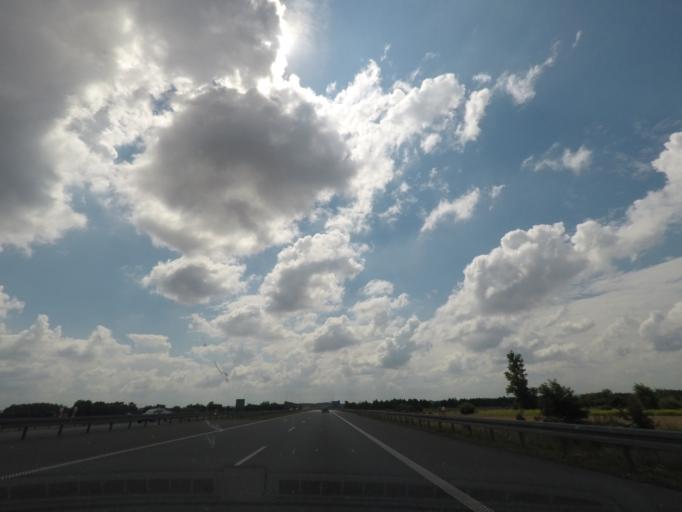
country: PL
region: Lodz Voivodeship
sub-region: Powiat zgierski
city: Strykow
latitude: 51.9109
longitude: 19.6231
